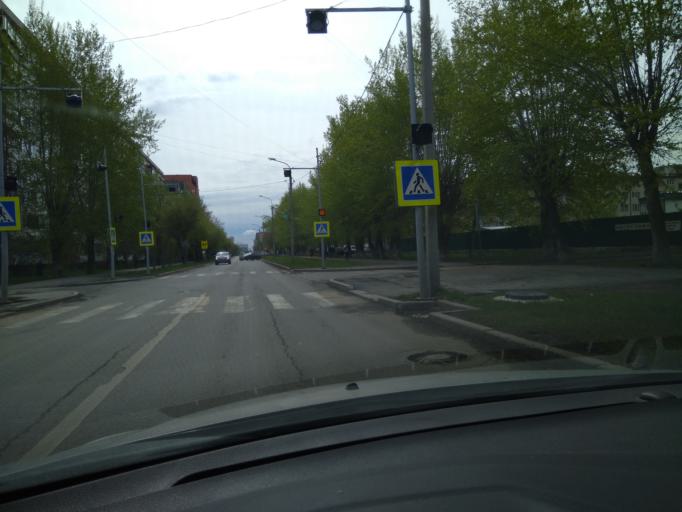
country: RU
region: Tjumen
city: Tyumen
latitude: 57.1384
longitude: 65.5894
